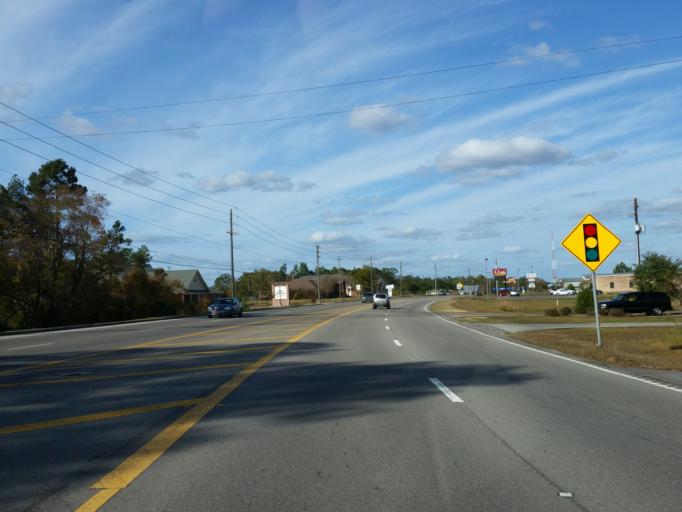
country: US
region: Mississippi
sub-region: Forrest County
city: Hattiesburg
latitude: 31.2959
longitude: -89.3241
